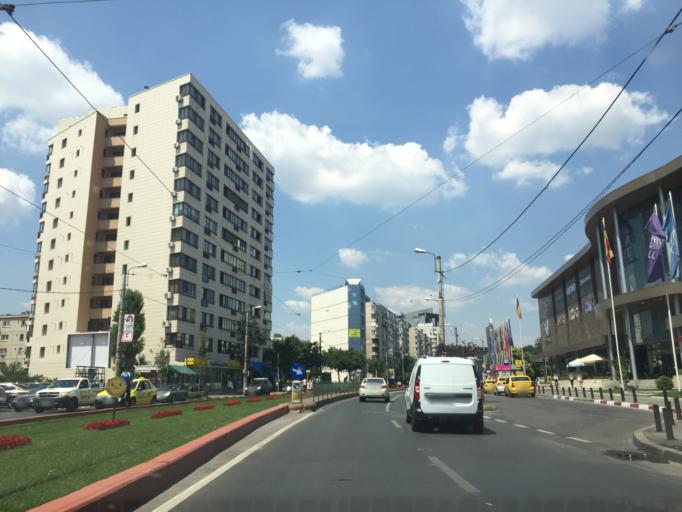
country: RO
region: Bucuresti
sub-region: Municipiul Bucuresti
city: Bucharest
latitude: 44.4195
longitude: 26.1265
